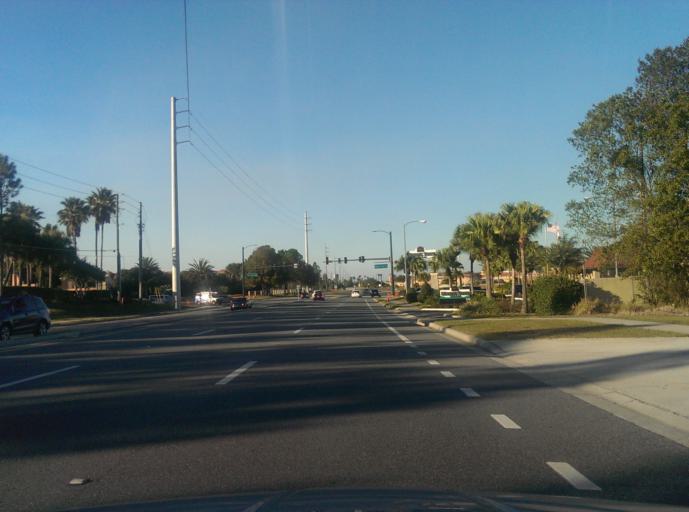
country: US
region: Florida
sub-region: Polk County
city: Citrus Ridge
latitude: 28.3278
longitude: -81.5907
